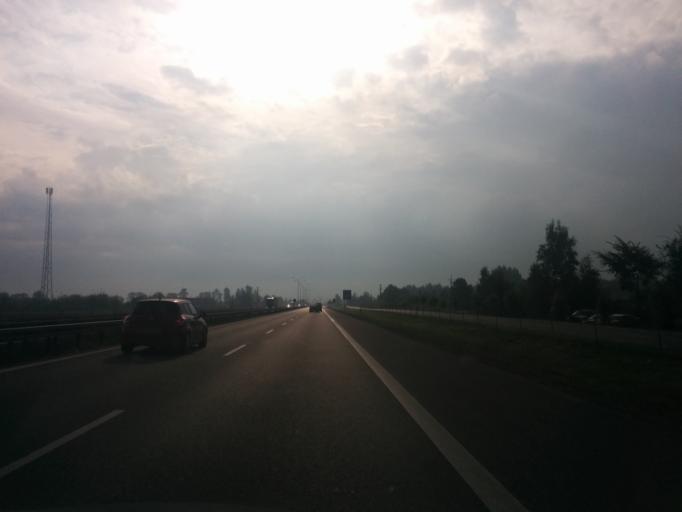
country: PL
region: Masovian Voivodeship
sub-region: Powiat radomski
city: Jedlinsk
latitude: 51.5250
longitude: 21.0952
